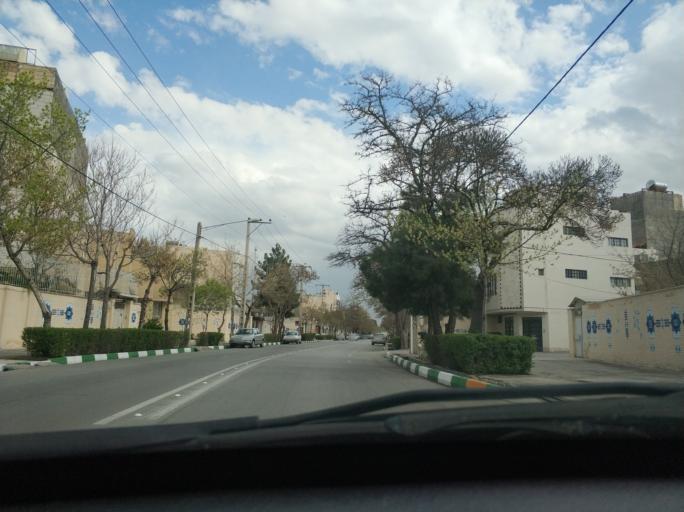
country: IR
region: Razavi Khorasan
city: Mashhad
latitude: 36.2772
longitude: 59.5894
